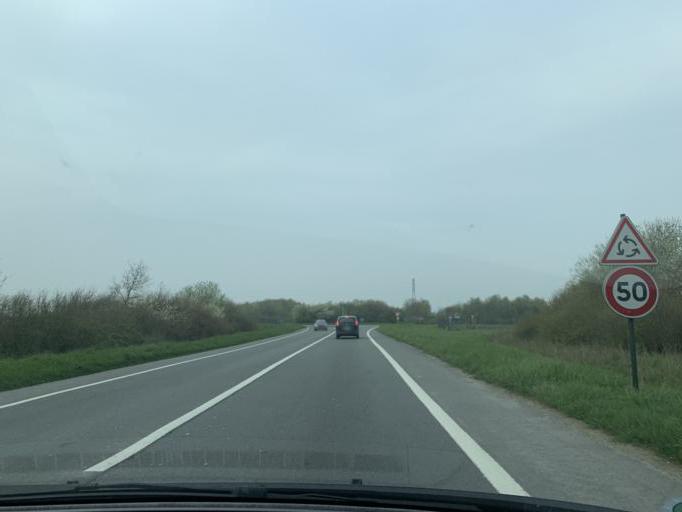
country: FR
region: Nord-Pas-de-Calais
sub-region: Departement du Pas-de-Calais
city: Montreuil
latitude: 50.4322
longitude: 1.7351
